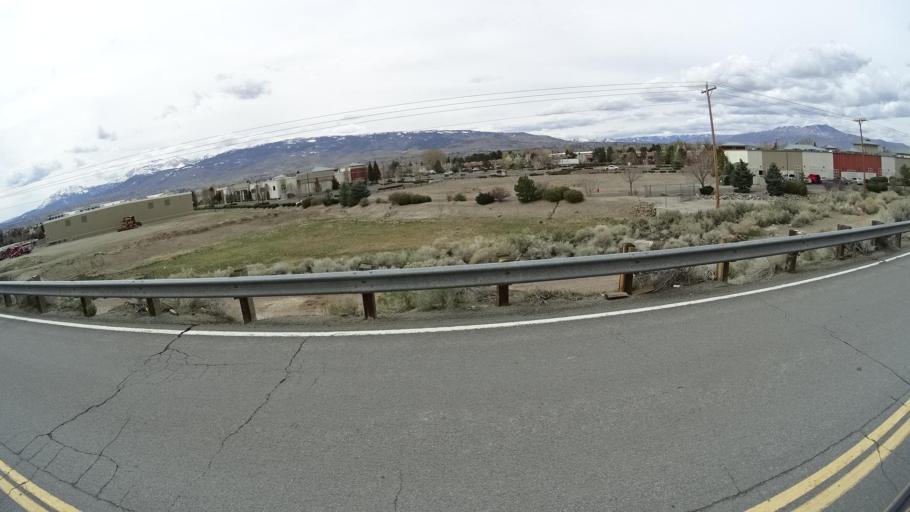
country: US
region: Nevada
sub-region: Washoe County
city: Sparks
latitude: 39.4725
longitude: -119.7630
